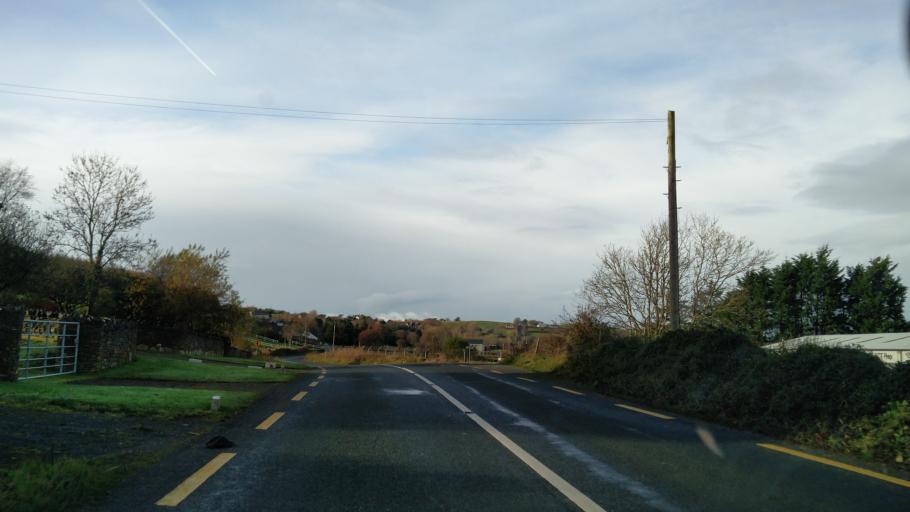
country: IE
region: Connaught
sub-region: Maigh Eo
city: Westport
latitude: 53.7873
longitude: -9.4933
